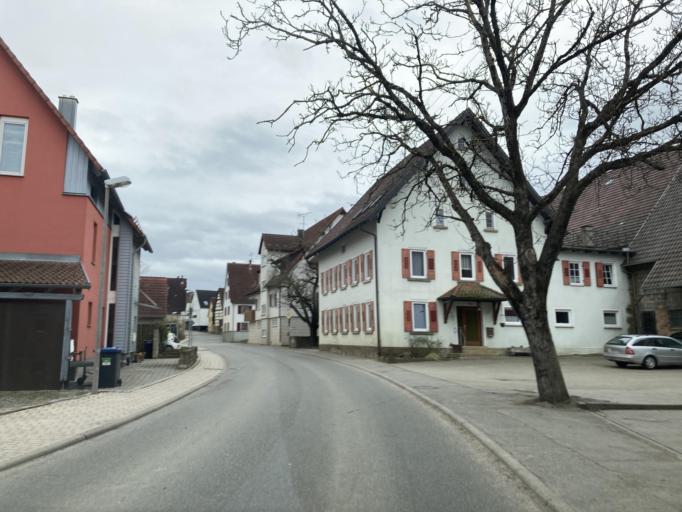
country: DE
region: Baden-Wuerttemberg
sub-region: Regierungsbezirk Stuttgart
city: Bondorf
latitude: 48.4887
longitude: 8.8464
